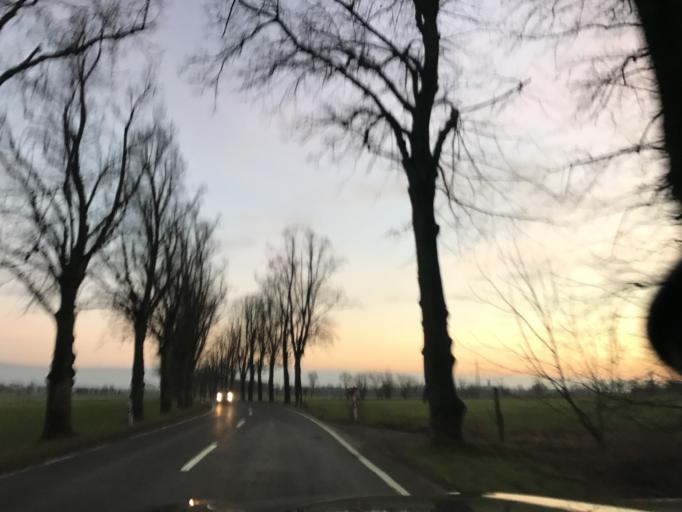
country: DE
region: Brandenburg
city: Ketzin
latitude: 52.5027
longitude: 12.8494
